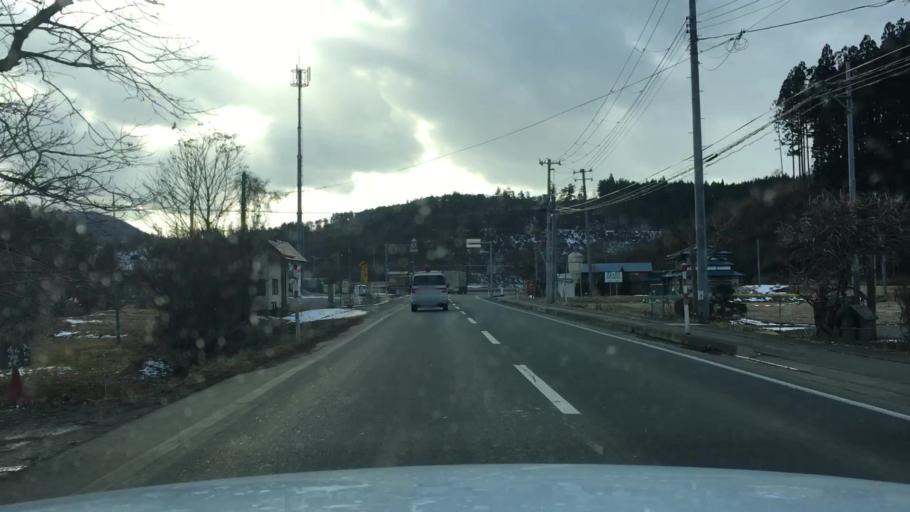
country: JP
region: Iwate
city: Morioka-shi
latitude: 39.6738
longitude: 141.2149
